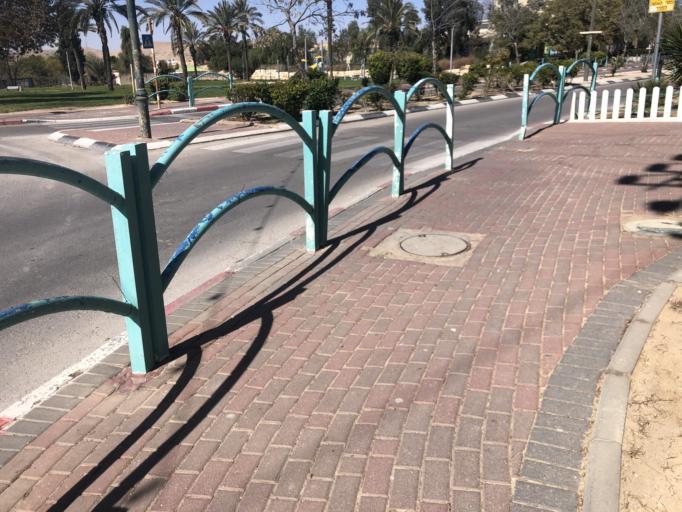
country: IL
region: Southern District
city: Dimona
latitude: 31.0666
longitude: 35.0400
